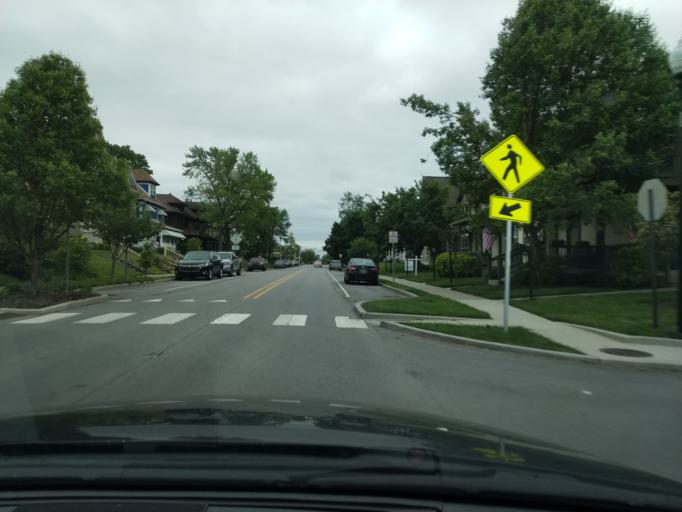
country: US
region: Indiana
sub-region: Marion County
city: Indianapolis
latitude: 39.7994
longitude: -86.1495
